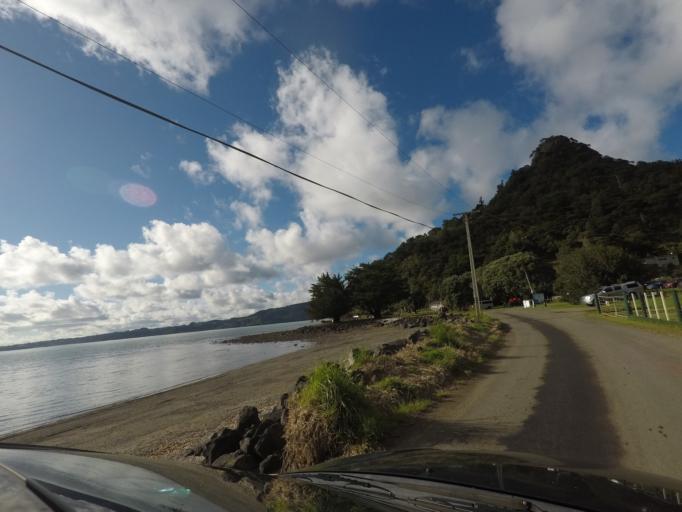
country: NZ
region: Auckland
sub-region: Auckland
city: Titirangi
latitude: -37.0155
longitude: 174.5583
